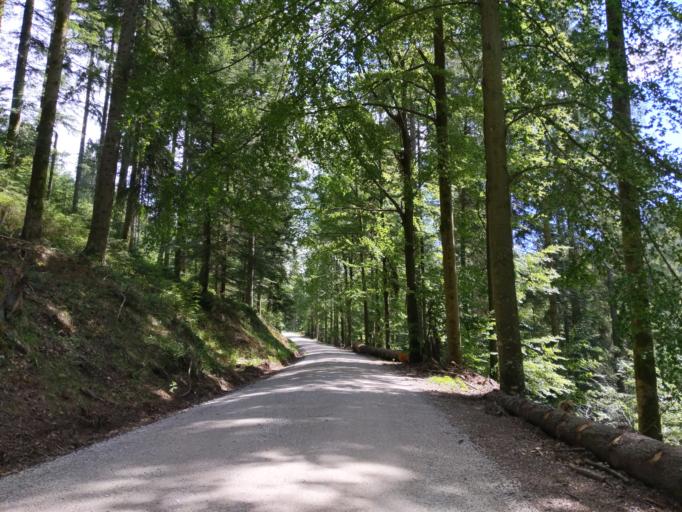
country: DE
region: Baden-Wuerttemberg
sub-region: Karlsruhe Region
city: Bad Rippoldsau-Schapbach
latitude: 48.4153
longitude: 8.3632
